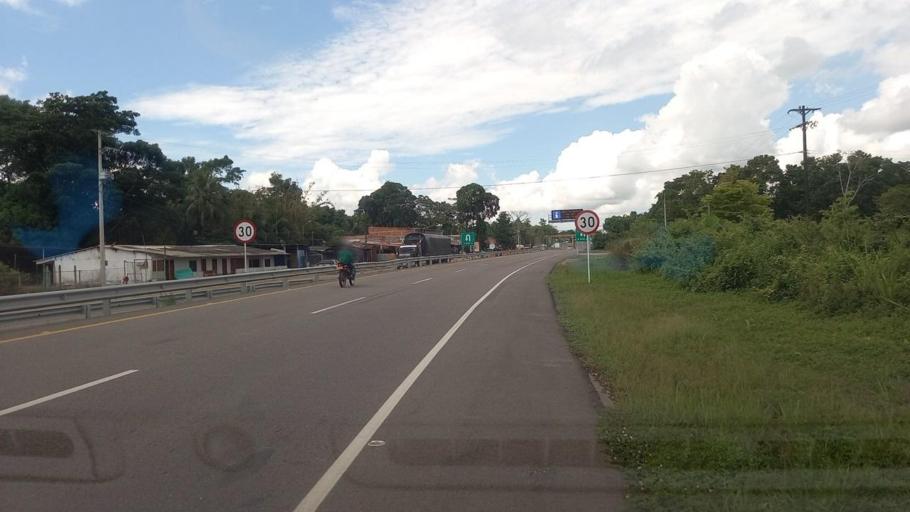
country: CO
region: Santander
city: Sabana de Torres
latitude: 7.1341
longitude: -73.5515
